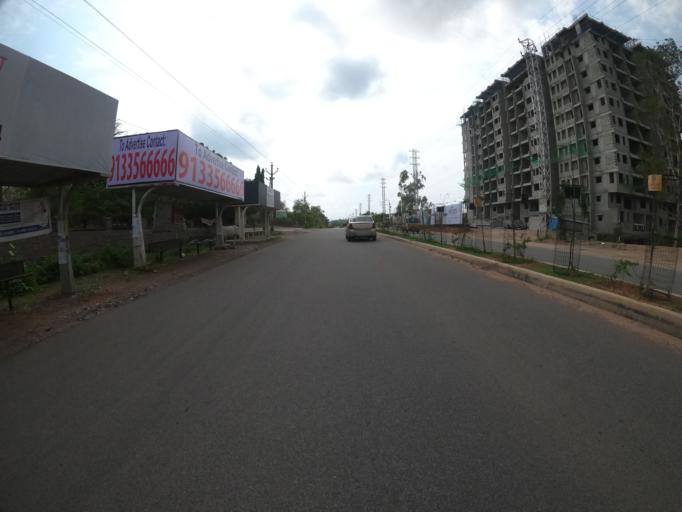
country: IN
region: Telangana
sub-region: Medak
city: Serilingampalle
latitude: 17.3918
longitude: 78.3231
